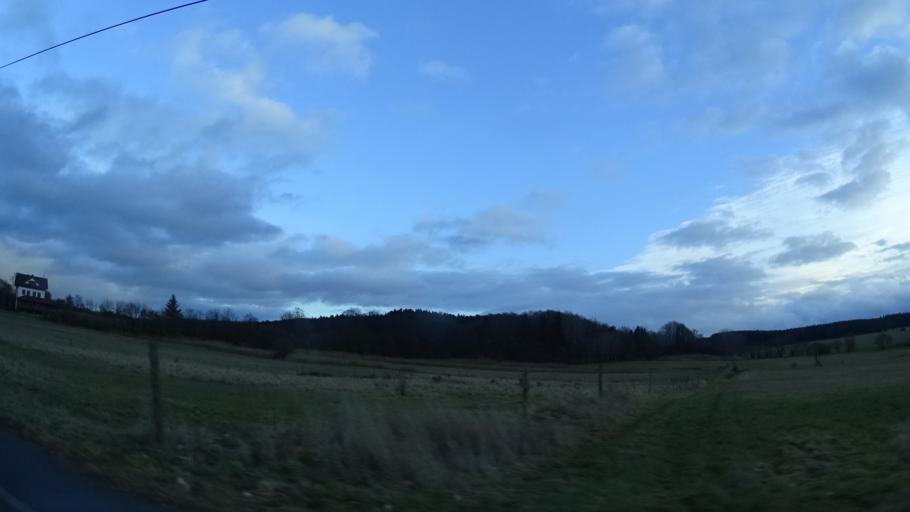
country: DE
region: Thuringia
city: Stadtilm
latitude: 50.7289
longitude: 11.0630
